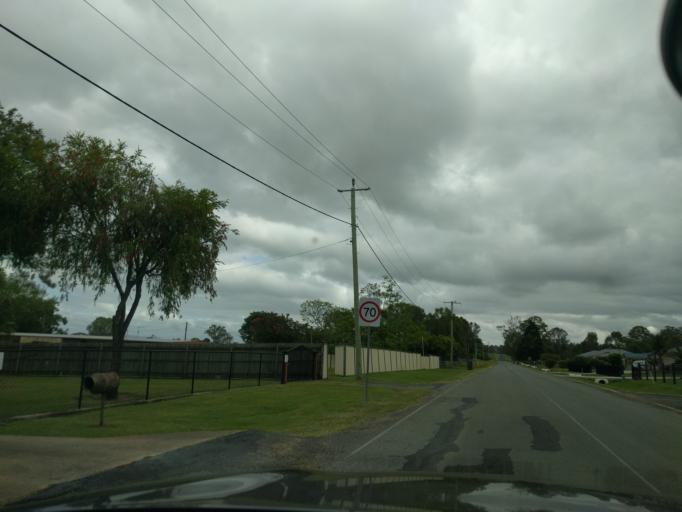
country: AU
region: Queensland
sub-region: Logan
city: Cedar Vale
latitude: -28.0192
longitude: 153.0099
